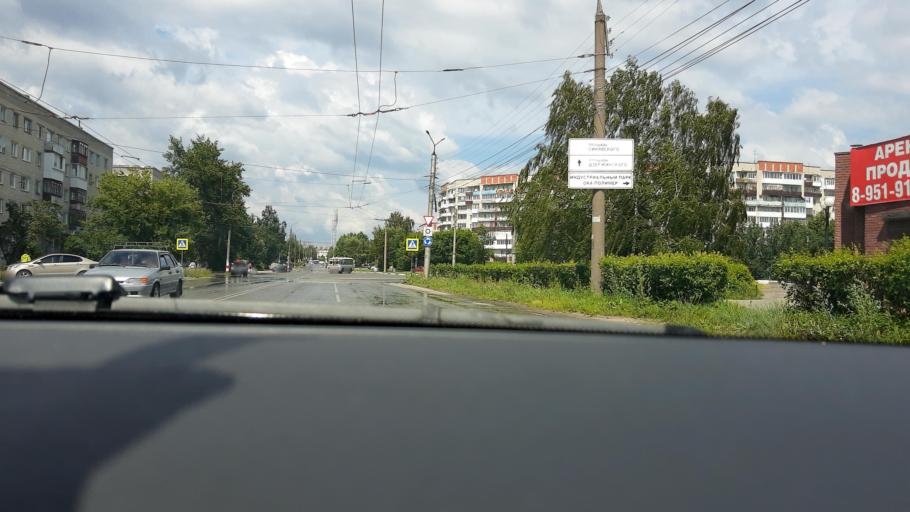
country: RU
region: Nizjnij Novgorod
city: Dzerzhinsk
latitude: 56.2301
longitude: 43.4571
